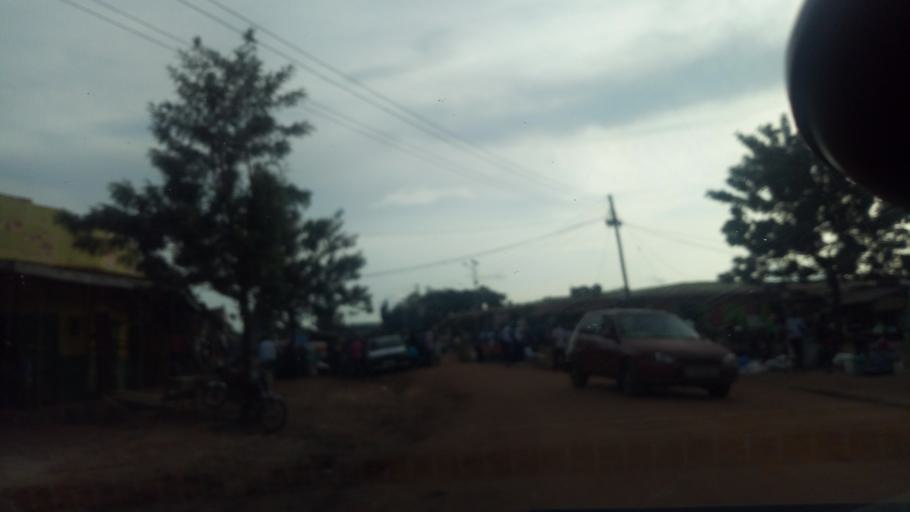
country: UG
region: Western Region
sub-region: Kiryandongo District
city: Kiryandongo
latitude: 1.8112
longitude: 32.0095
